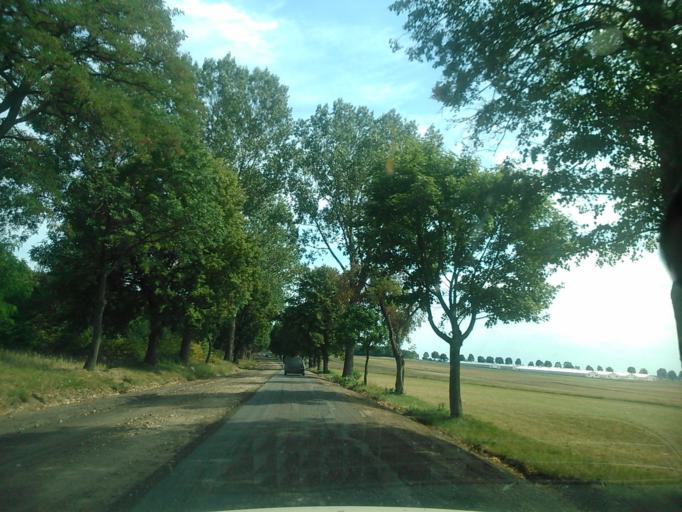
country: PL
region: Warmian-Masurian Voivodeship
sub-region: Powiat dzialdowski
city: Ilowo -Osada
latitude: 53.1962
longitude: 20.2545
